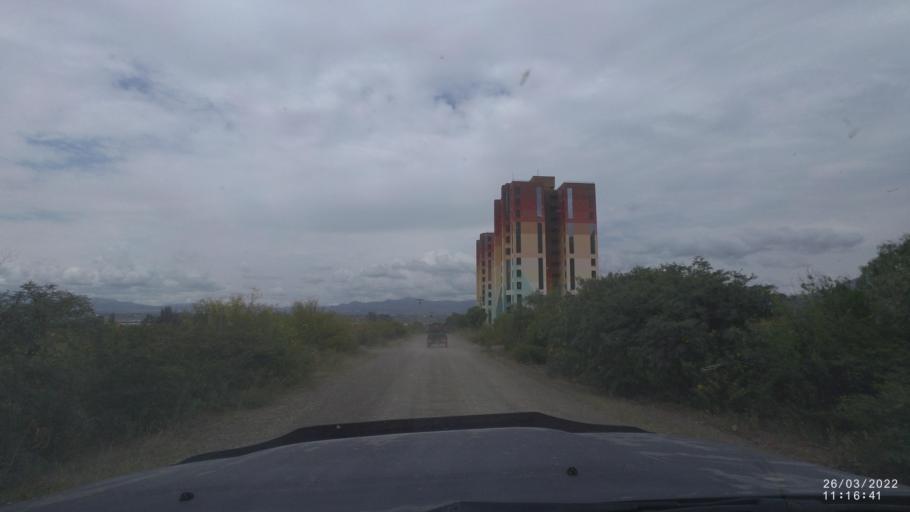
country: BO
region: Cochabamba
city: Tarata
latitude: -17.5360
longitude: -66.0234
